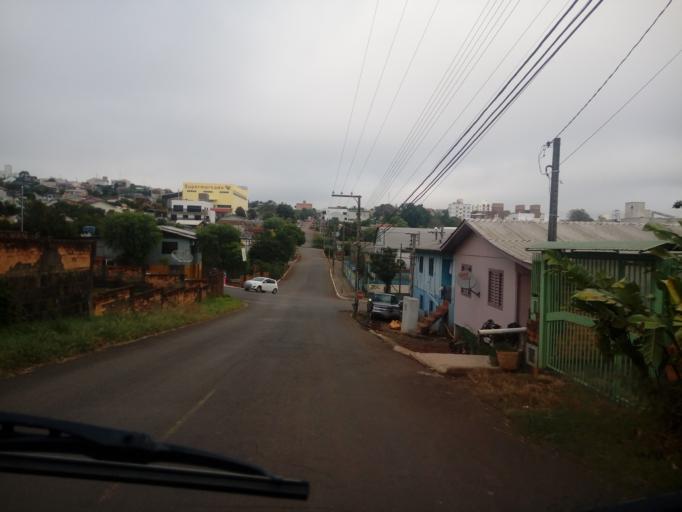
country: BR
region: Santa Catarina
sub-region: Chapeco
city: Chapeco
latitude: -27.1162
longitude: -52.6239
